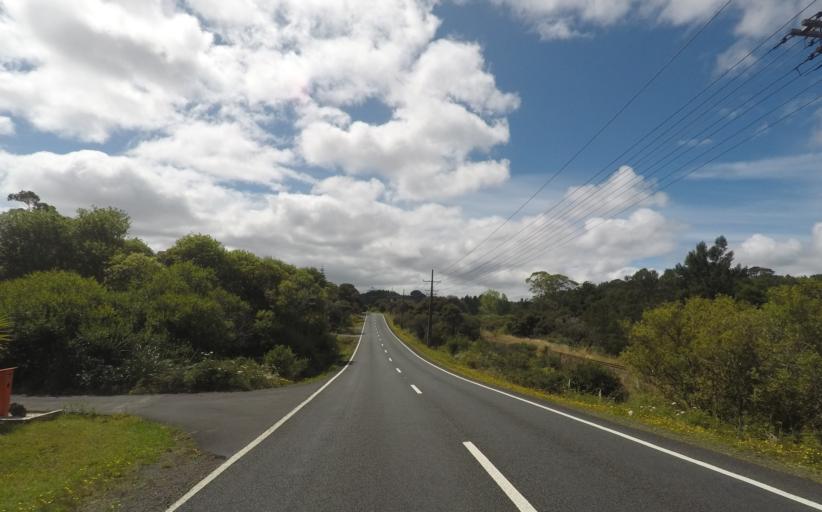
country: NZ
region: Auckland
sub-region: Auckland
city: Muriwai Beach
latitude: -36.8556
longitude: 174.5452
